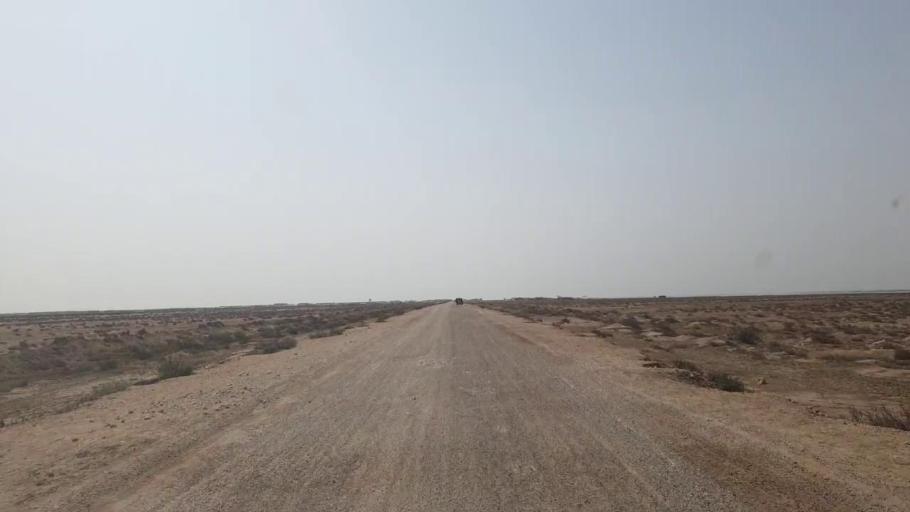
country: PK
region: Sindh
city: Jati
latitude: 24.3503
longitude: 68.5937
